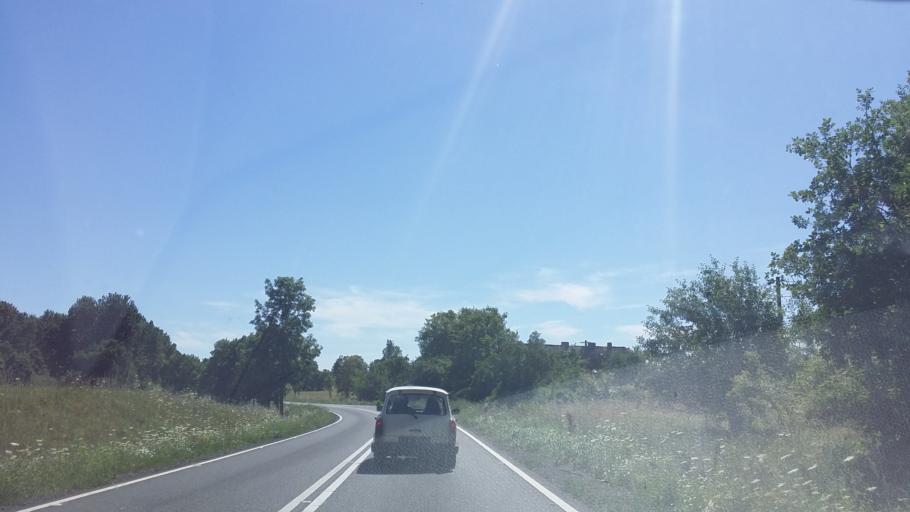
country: PL
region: West Pomeranian Voivodeship
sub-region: Powiat stargardzki
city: Insko
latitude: 53.4722
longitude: 15.5778
